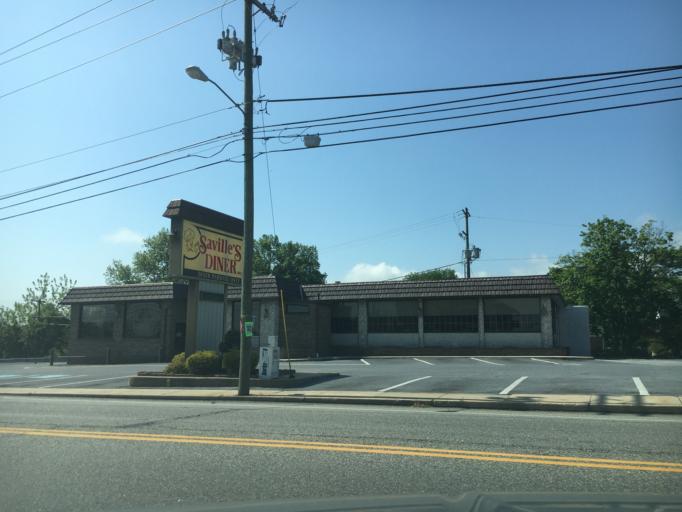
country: US
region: Pennsylvania
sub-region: Berks County
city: Boyertown
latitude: 40.3276
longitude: -75.6248
